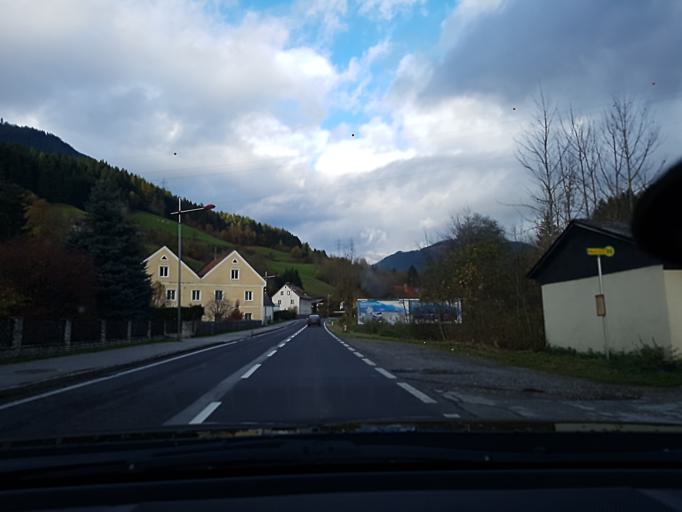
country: AT
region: Styria
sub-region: Politischer Bezirk Liezen
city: Liezen
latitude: 47.5722
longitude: 14.2460
